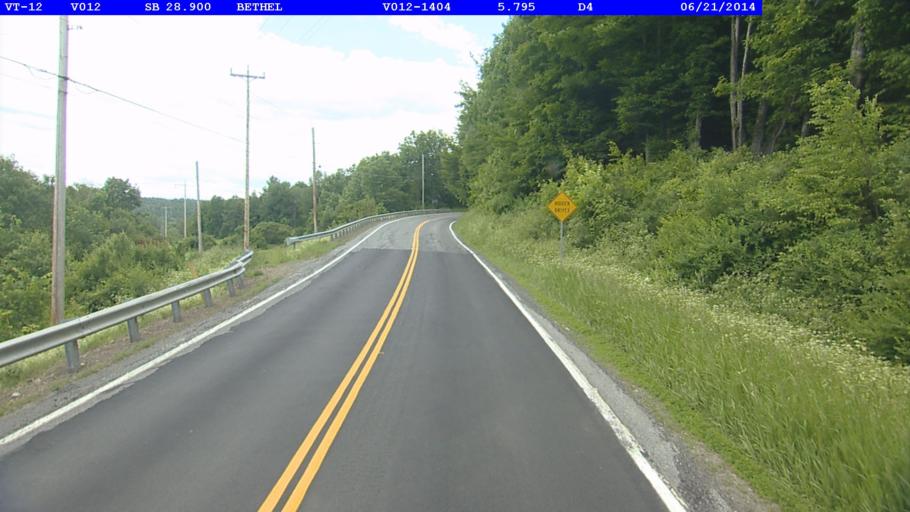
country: US
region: Vermont
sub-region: Orange County
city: Randolph
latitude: 43.8791
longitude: -72.6467
